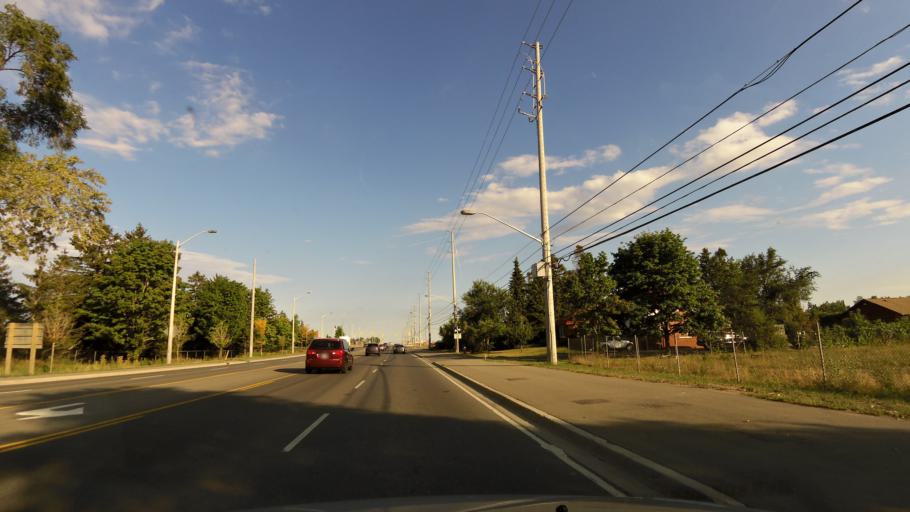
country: CA
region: Ontario
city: Brampton
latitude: 43.6392
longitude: -79.7922
